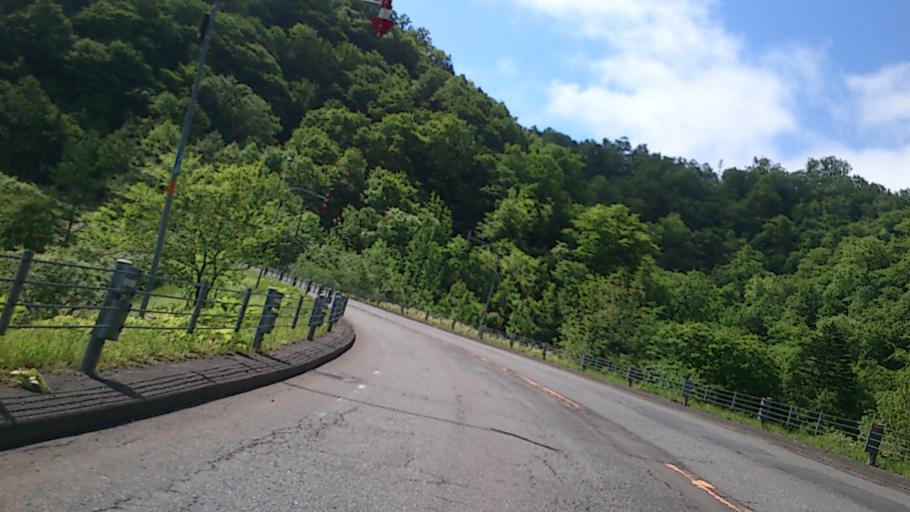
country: JP
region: Hokkaido
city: Shiraoi
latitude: 42.7166
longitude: 141.1985
